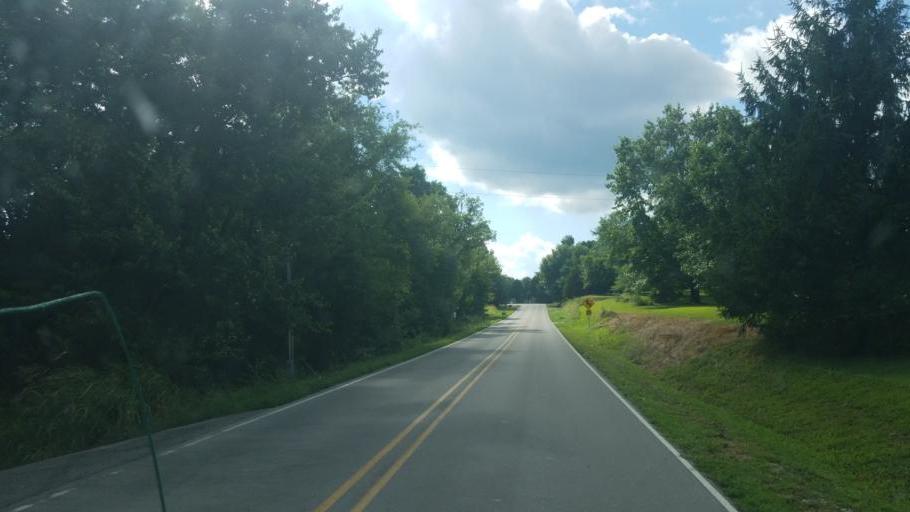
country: US
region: Illinois
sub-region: Union County
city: Cobden
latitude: 37.5476
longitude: -89.2860
